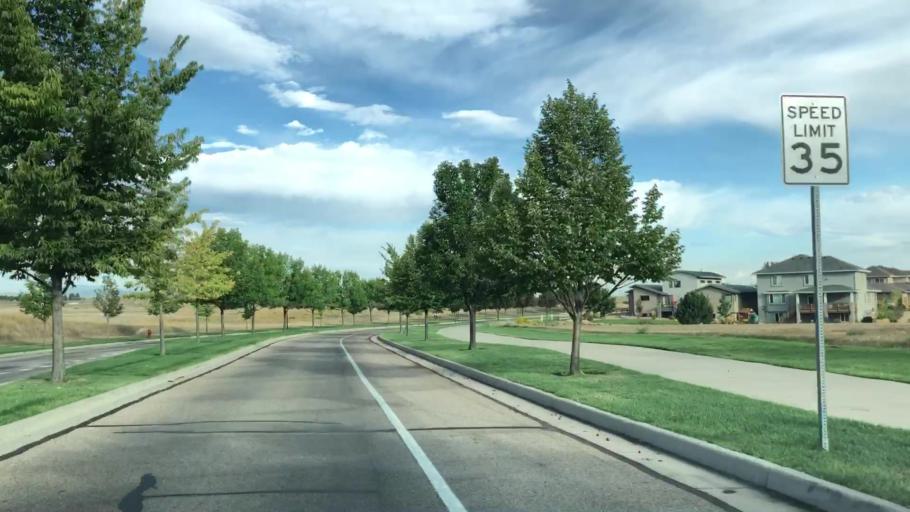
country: US
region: Colorado
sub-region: Weld County
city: Windsor
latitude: 40.4471
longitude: -104.9757
